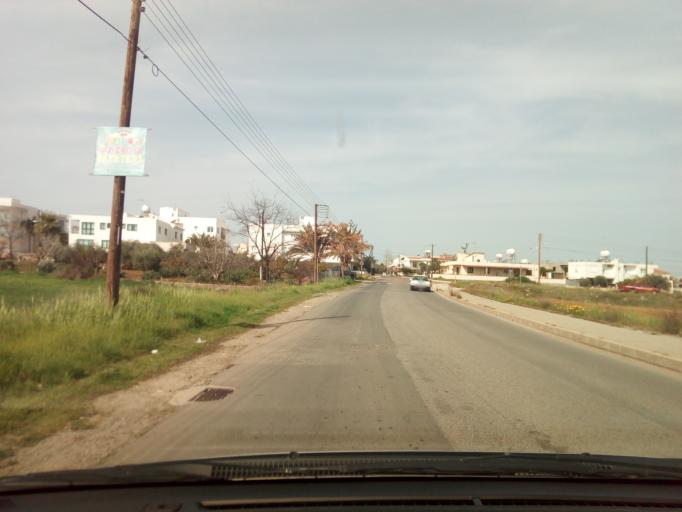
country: CY
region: Lefkosia
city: Tseri
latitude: 35.0997
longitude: 33.3110
